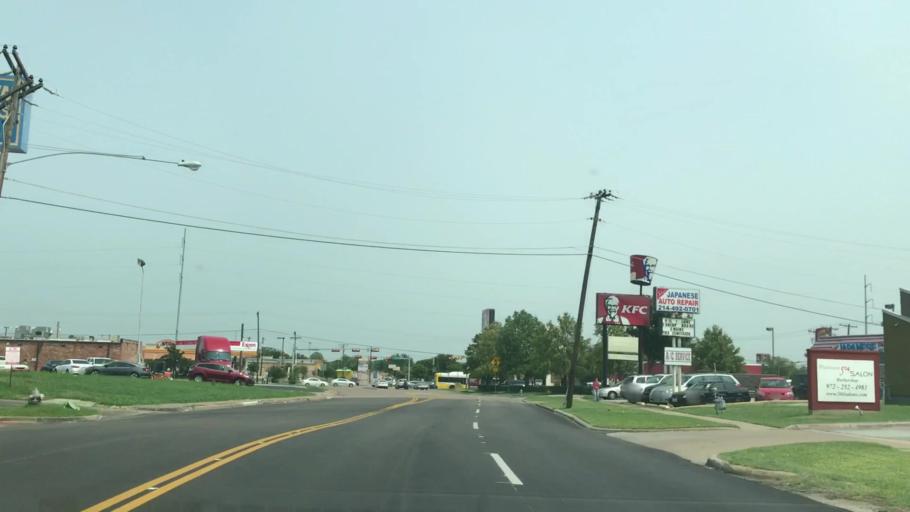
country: US
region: Texas
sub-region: Dallas County
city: Irving
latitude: 32.8477
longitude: -96.9941
